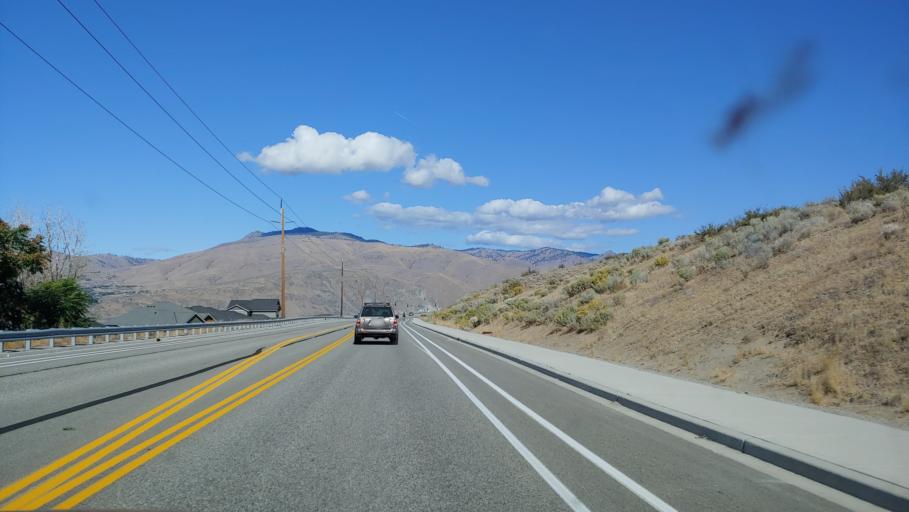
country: US
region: Washington
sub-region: Douglas County
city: East Wenatchee Bench
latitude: 47.4530
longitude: -120.2911
